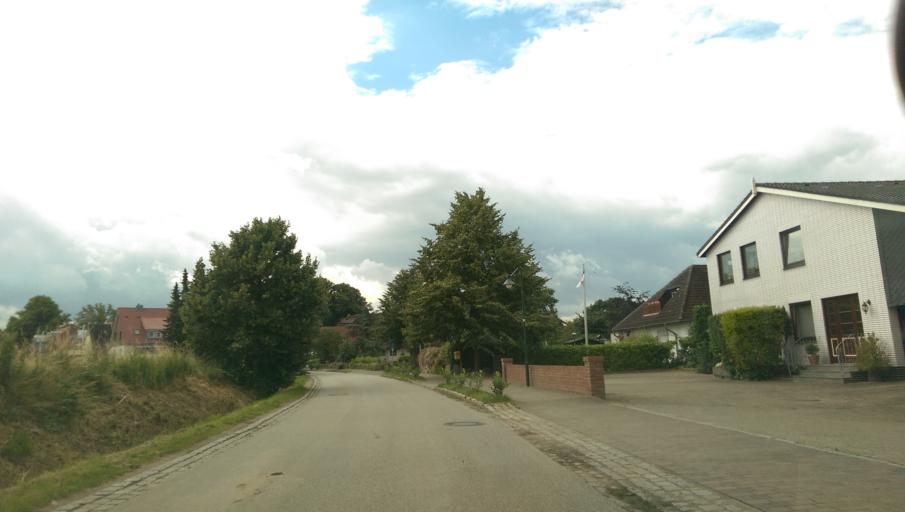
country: DE
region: Schleswig-Holstein
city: Travemuende
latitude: 53.9696
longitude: 10.8217
